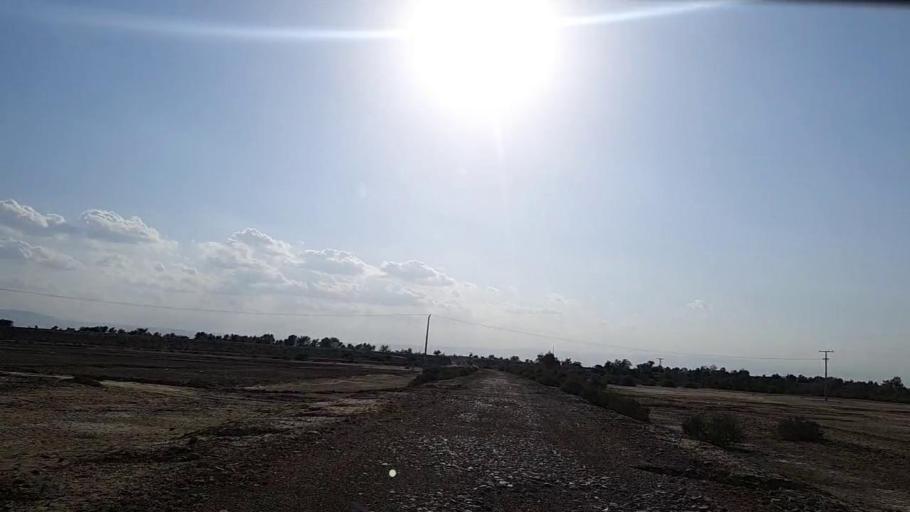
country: PK
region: Sindh
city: Johi
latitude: 26.5854
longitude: 67.5445
